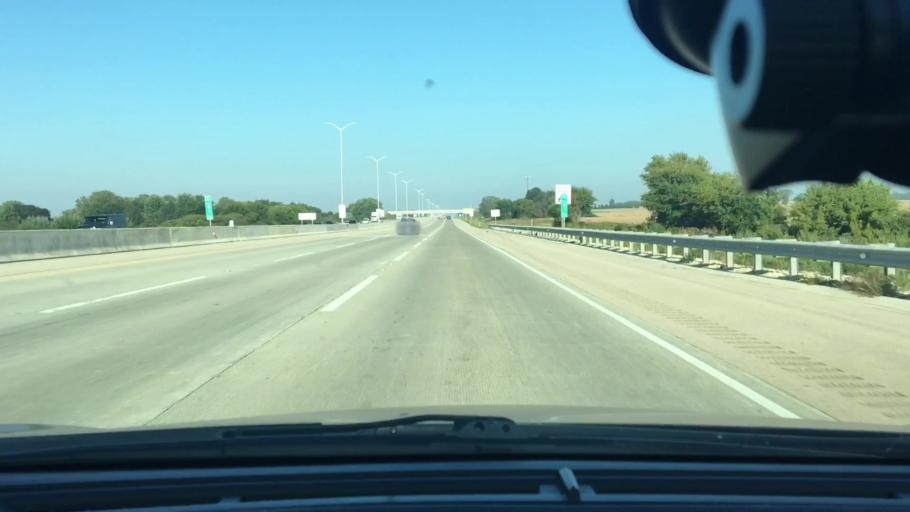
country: US
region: Illinois
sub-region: Kane County
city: Hampshire
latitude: 42.1489
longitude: -88.5247
